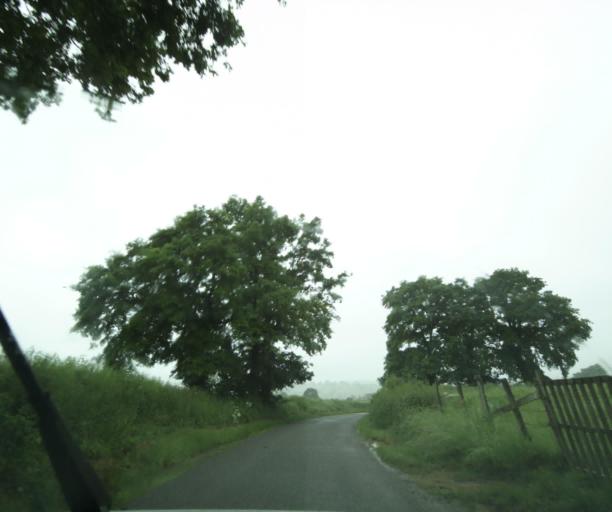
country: FR
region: Bourgogne
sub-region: Departement de Saone-et-Loire
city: Charolles
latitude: 46.4173
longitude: 4.2770
